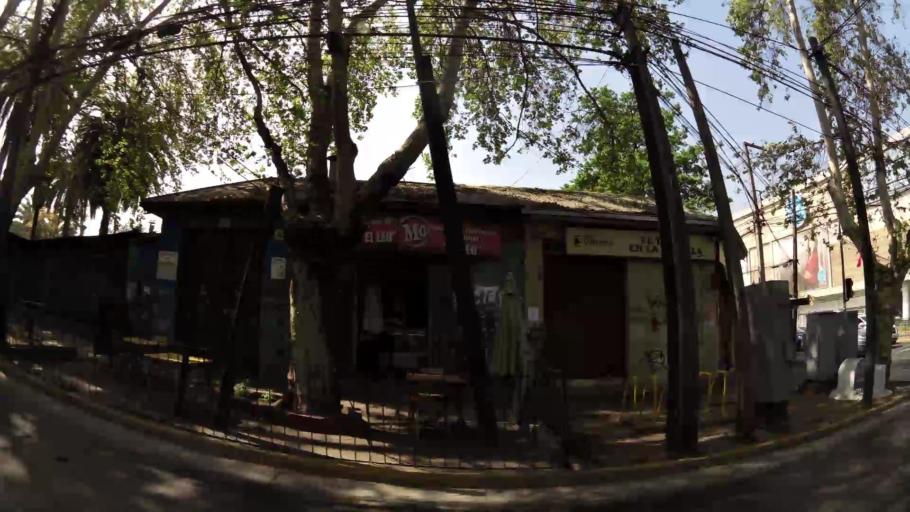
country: CL
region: Santiago Metropolitan
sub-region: Provincia de Santiago
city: Villa Presidente Frei, Nunoa, Santiago, Chile
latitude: -33.4642
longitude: -70.5982
